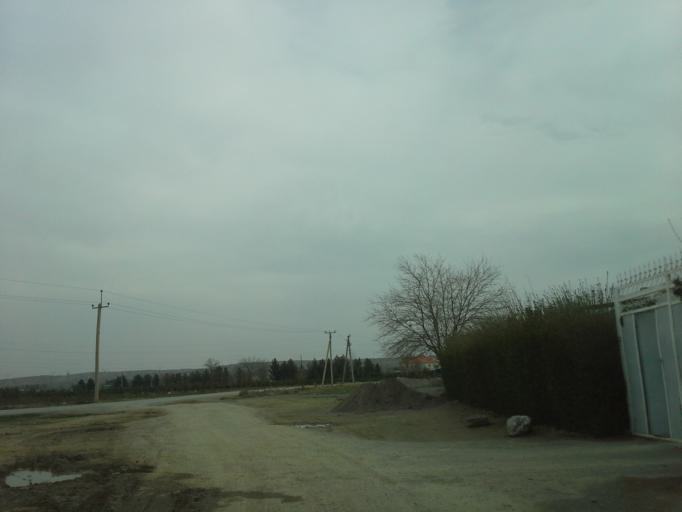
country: TM
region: Ahal
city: Abadan
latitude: 37.9720
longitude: 58.2302
